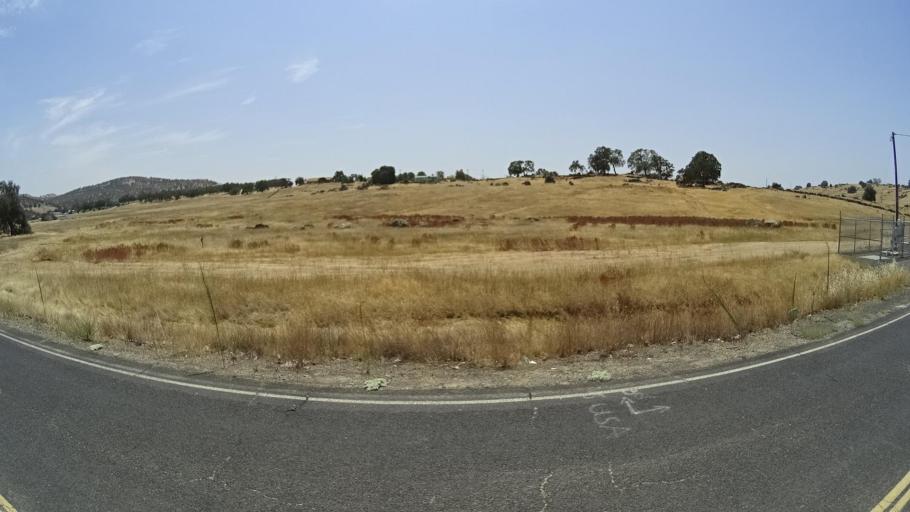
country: US
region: California
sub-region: Tuolumne County
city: Jamestown
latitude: 37.6471
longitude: -120.3255
